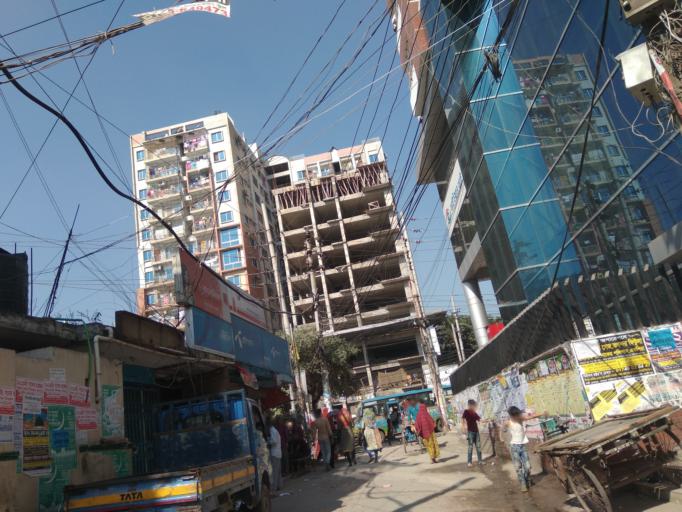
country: BD
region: Dhaka
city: Azimpur
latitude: 23.7731
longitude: 90.3613
